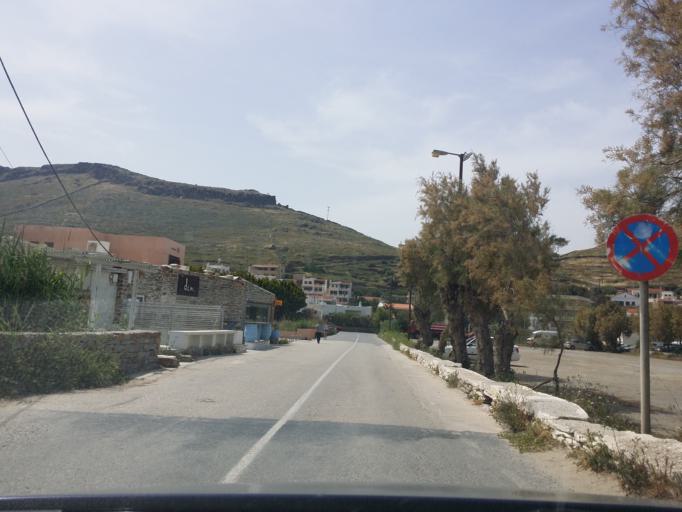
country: GR
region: South Aegean
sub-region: Nomos Kykladon
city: Kea
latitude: 37.6577
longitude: 24.3137
